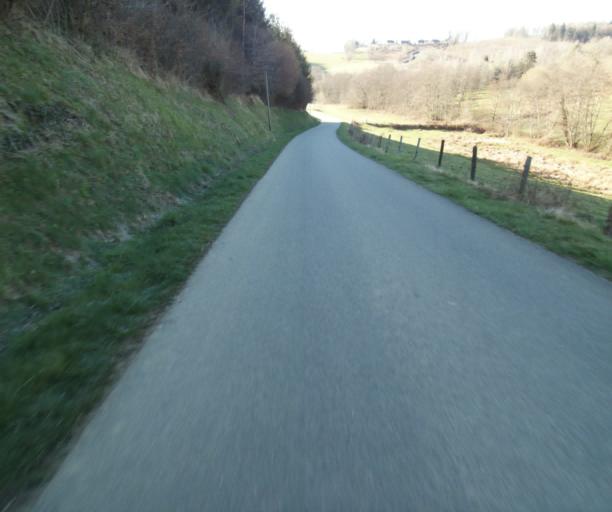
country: FR
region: Limousin
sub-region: Departement de la Correze
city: Seilhac
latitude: 45.3805
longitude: 1.7500
